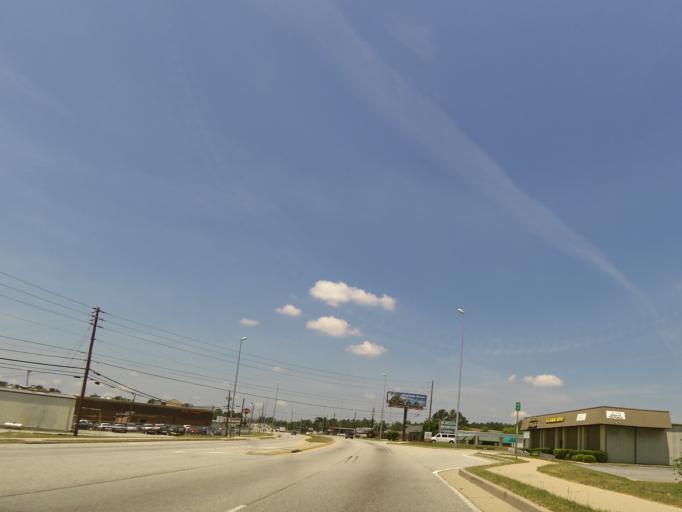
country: US
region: Georgia
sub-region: Bibb County
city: West Point
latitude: 32.8304
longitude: -83.7242
